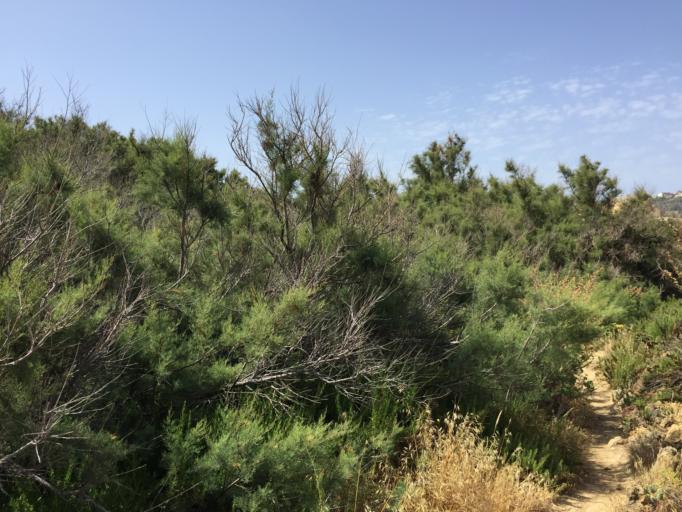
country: MT
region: In-Nadur
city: Nadur
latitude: 36.0629
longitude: 14.2871
